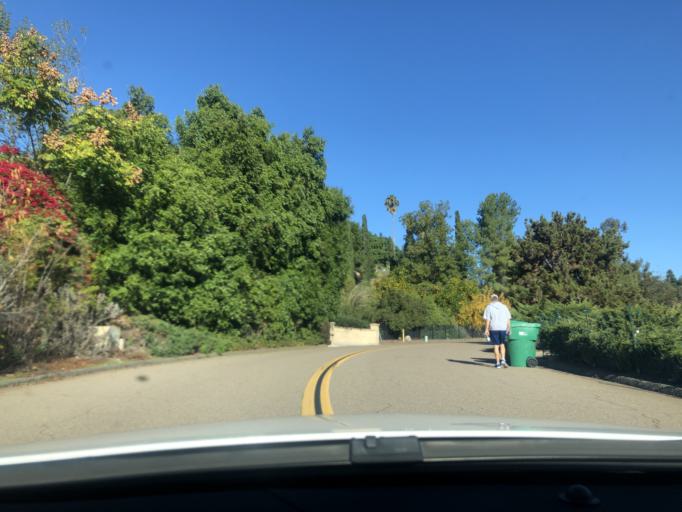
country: US
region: California
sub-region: San Diego County
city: Casa de Oro-Mount Helix
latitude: 32.7694
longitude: -116.9492
